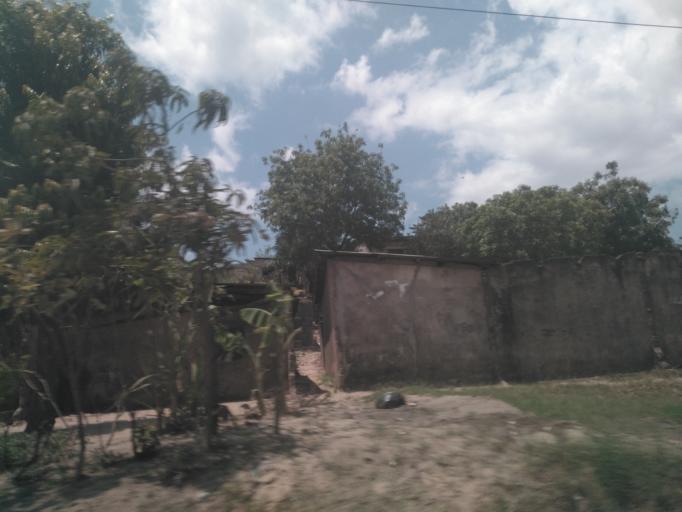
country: TZ
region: Dar es Salaam
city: Dar es Salaam
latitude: -6.8863
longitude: 39.2731
